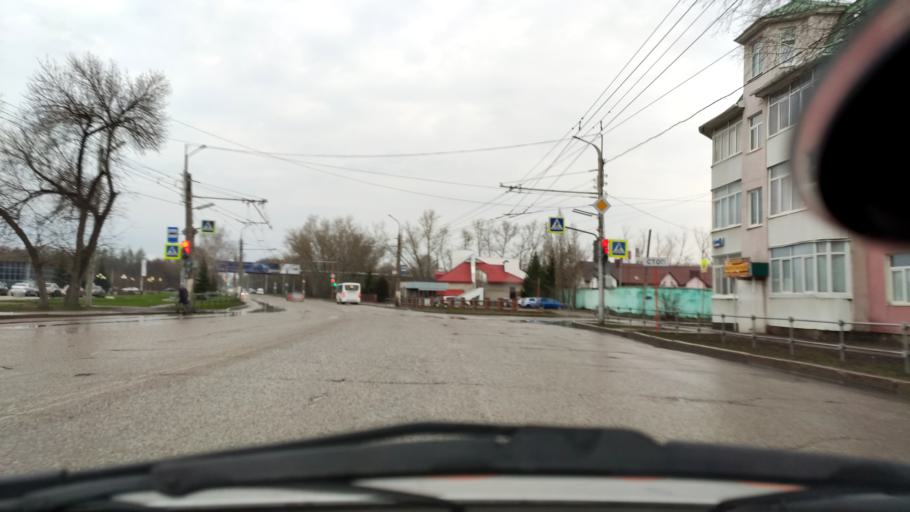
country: RU
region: Bashkortostan
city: Sterlitamak
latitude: 53.6539
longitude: 55.9482
